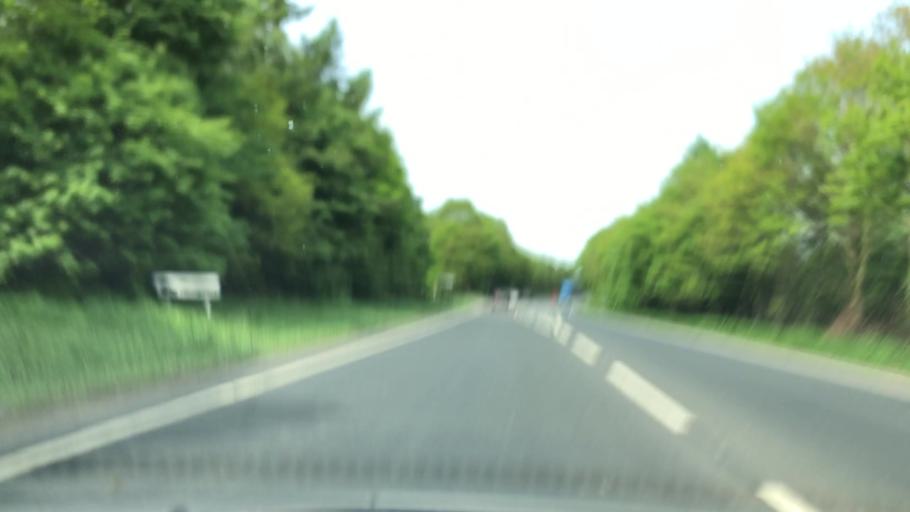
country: GB
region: England
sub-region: Shropshire
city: Gobowen
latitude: 52.8962
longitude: -3.0433
